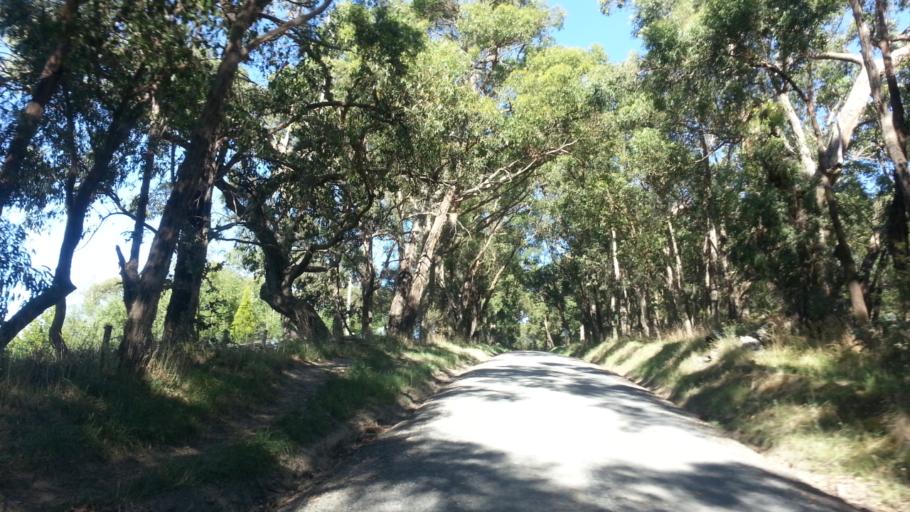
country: AU
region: Victoria
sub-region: Yarra Ranges
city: Belgrave Heights
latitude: -37.9470
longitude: 145.3650
